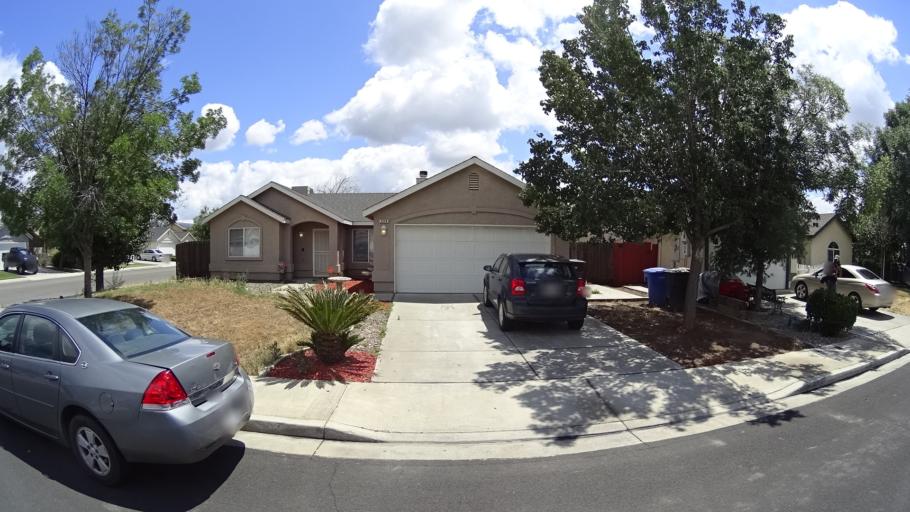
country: US
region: California
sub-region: Kings County
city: Lucerne
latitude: 36.3530
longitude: -119.6633
